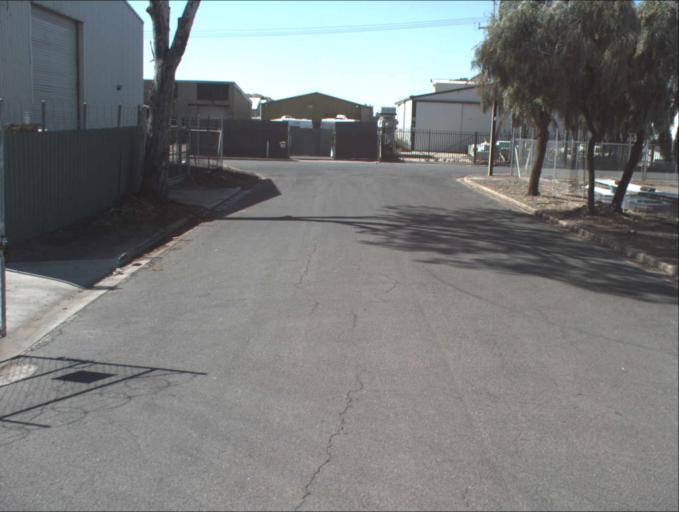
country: AU
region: South Australia
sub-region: Charles Sturt
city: Woodville North
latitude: -34.8356
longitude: 138.5599
